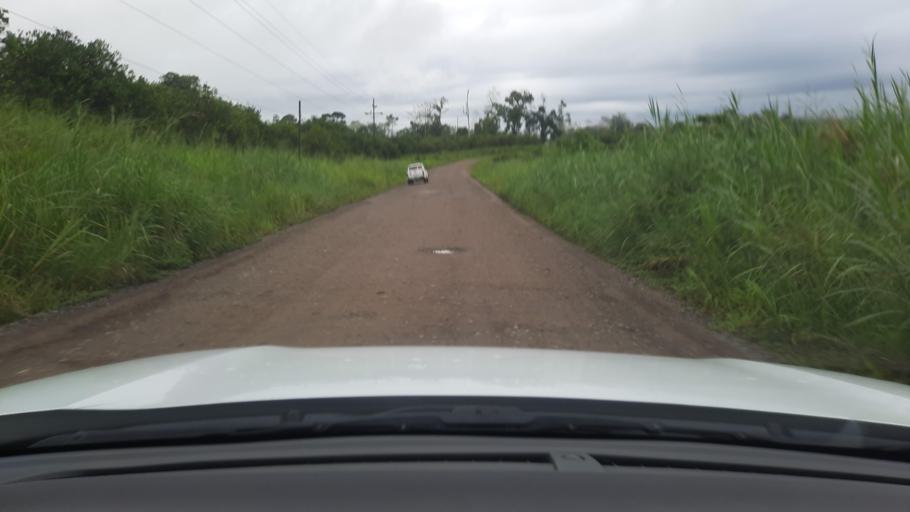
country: CR
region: Alajuela
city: San Jose
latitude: 10.9944
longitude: -85.2775
